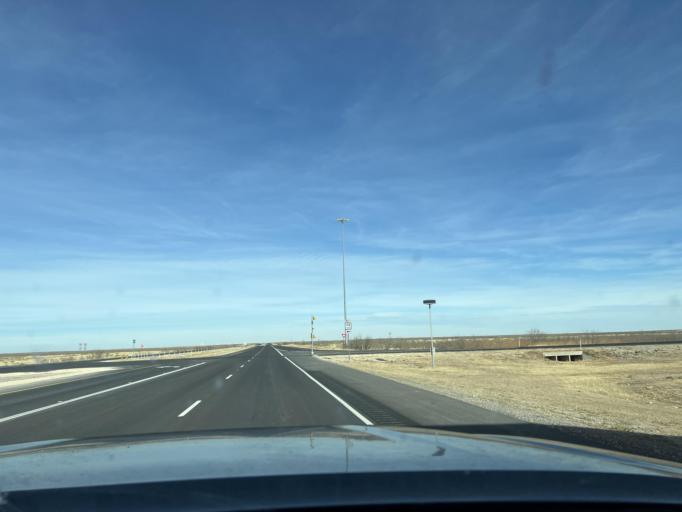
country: US
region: Texas
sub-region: Ector County
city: Gardendale
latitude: 32.0240
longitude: -102.4304
